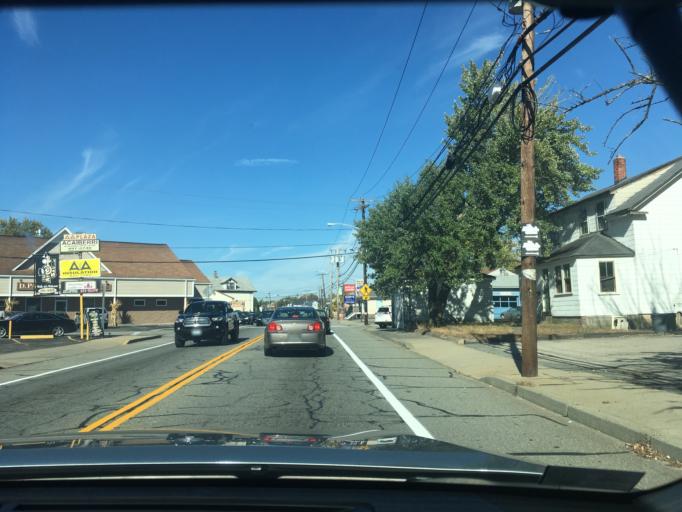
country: US
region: Rhode Island
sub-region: Providence County
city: North Providence
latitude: 41.8283
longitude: -71.4726
